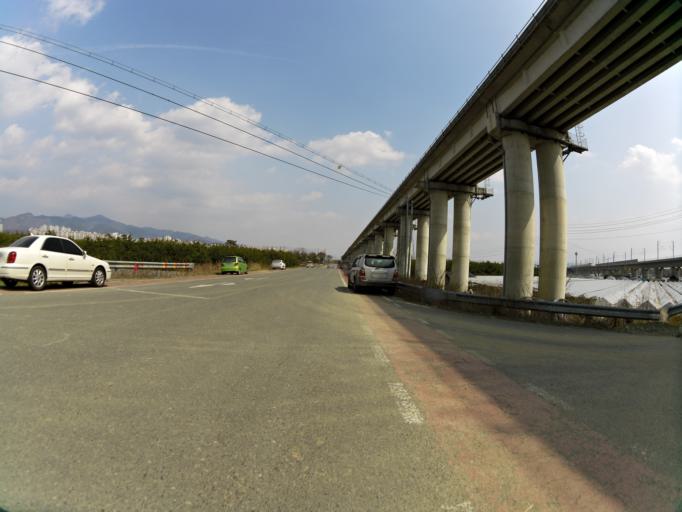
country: KR
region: Gyeongsangbuk-do
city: Gyeongsan-si
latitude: 35.8551
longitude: 128.7189
